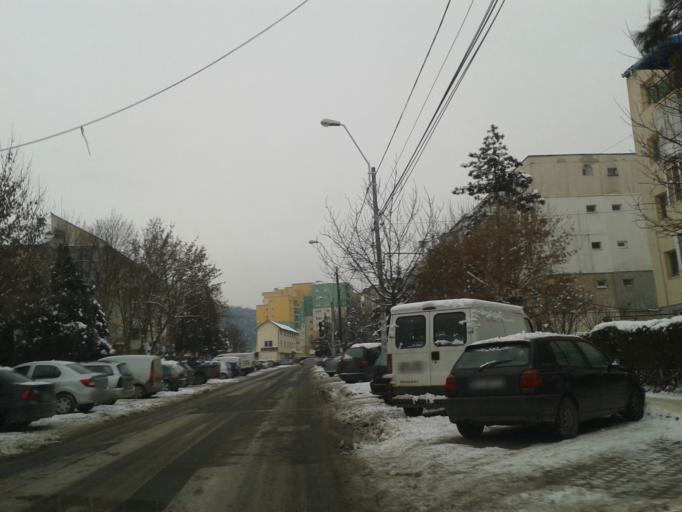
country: RO
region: Hunedoara
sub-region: Municipiul Deva
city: Deva
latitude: 45.8596
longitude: 22.9078
